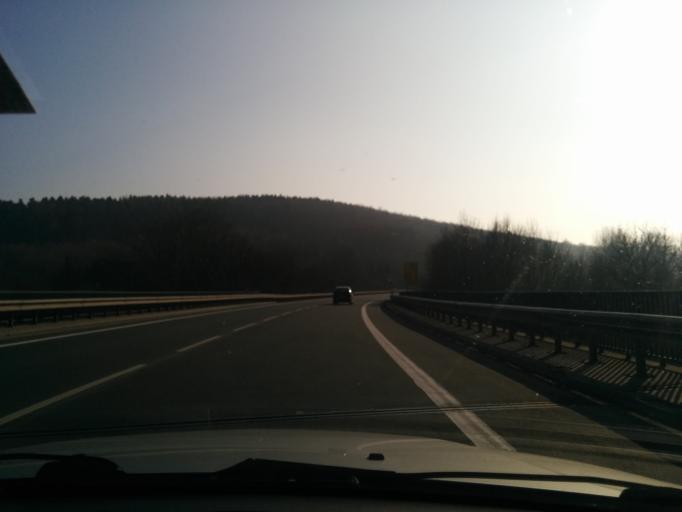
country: DE
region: North Rhine-Westphalia
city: Brakel
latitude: 51.7018
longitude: 9.1710
